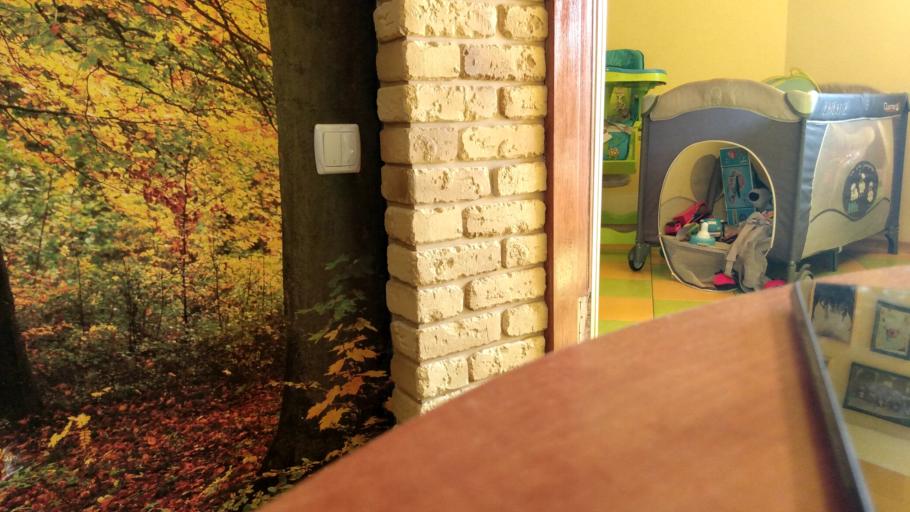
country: RU
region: Tverskaya
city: Sakharovo
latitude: 56.8872
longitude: 36.0828
